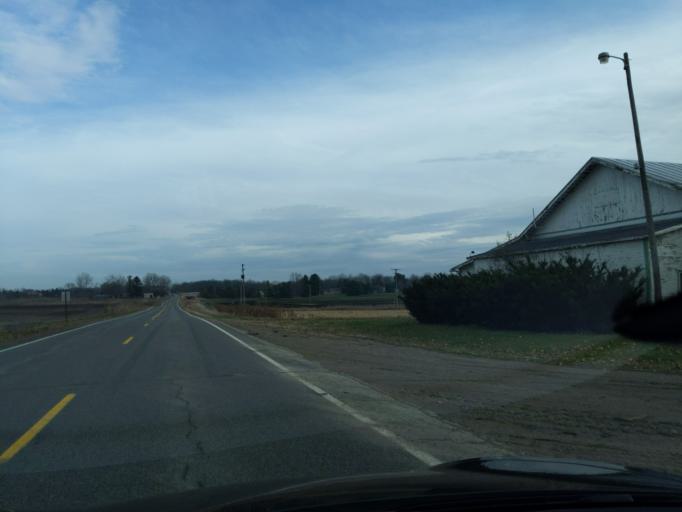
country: US
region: Michigan
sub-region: Ingham County
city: Mason
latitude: 42.6400
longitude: -84.4099
